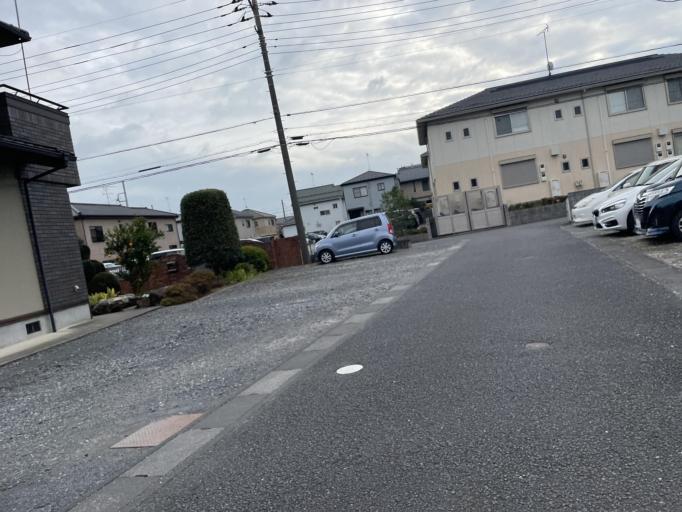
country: JP
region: Saitama
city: Shiraoka
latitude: 36.0162
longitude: 139.6631
